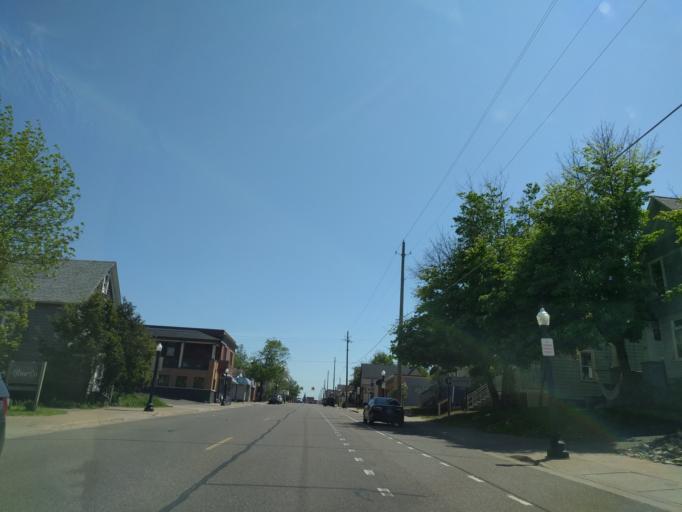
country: US
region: Michigan
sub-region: Marquette County
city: Marquette
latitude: 46.5510
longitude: -87.3948
